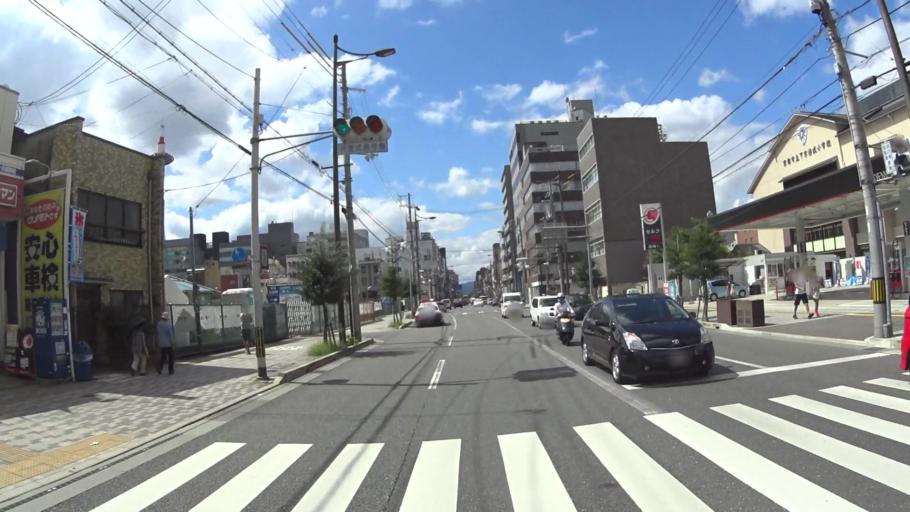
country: JP
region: Kyoto
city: Kyoto
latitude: 34.9892
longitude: 135.7628
